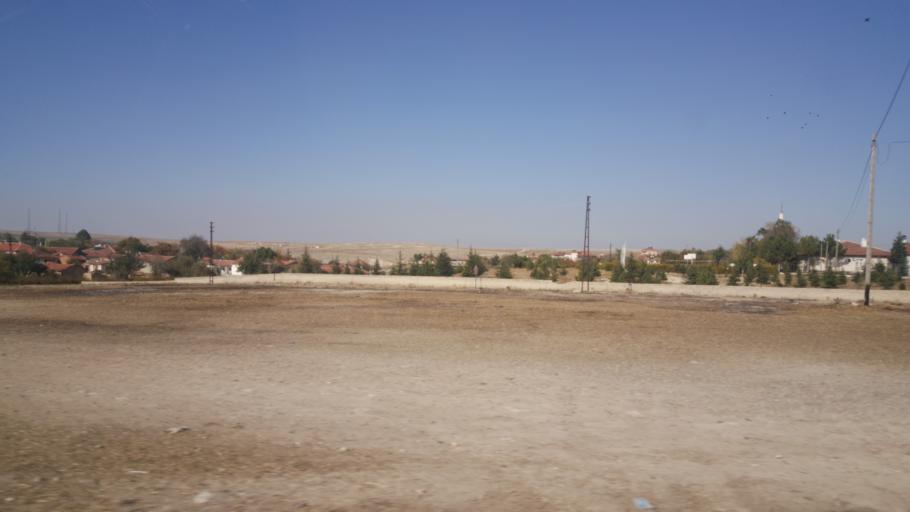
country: TR
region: Konya
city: Celtik
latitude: 39.0583
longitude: 31.8442
